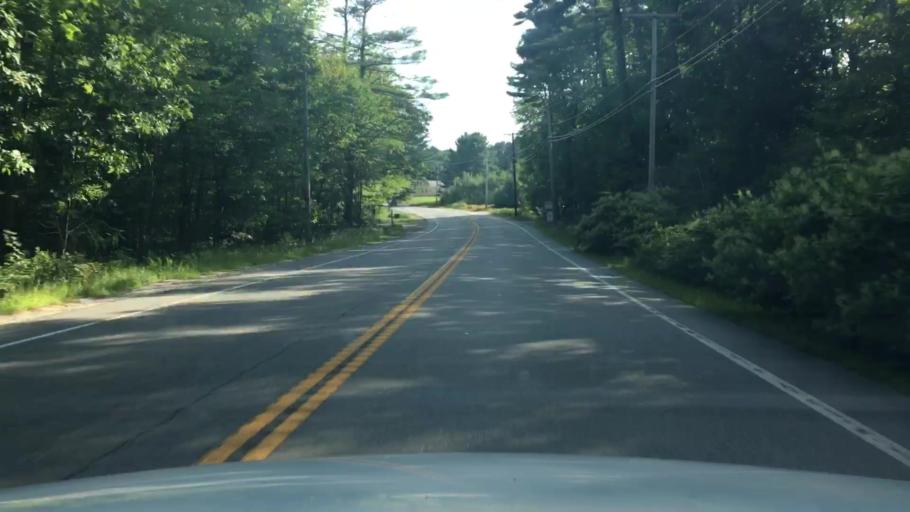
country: US
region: Maine
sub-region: Cumberland County
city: New Gloucester
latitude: 43.9328
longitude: -70.3083
